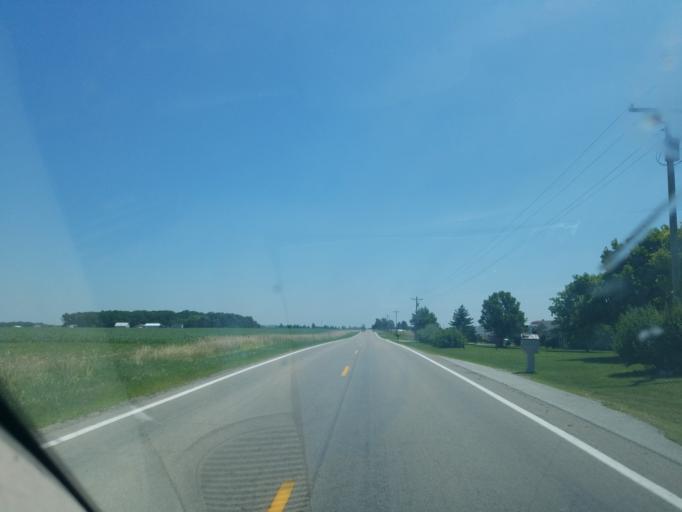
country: US
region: Ohio
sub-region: Mercer County
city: Rockford
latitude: 40.7423
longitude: -84.6961
